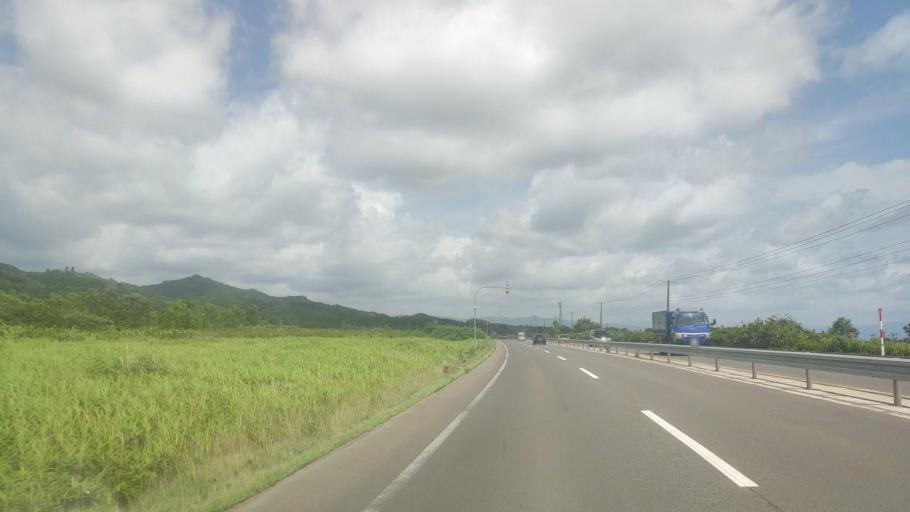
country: JP
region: Hokkaido
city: Niseko Town
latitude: 42.4495
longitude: 140.3309
